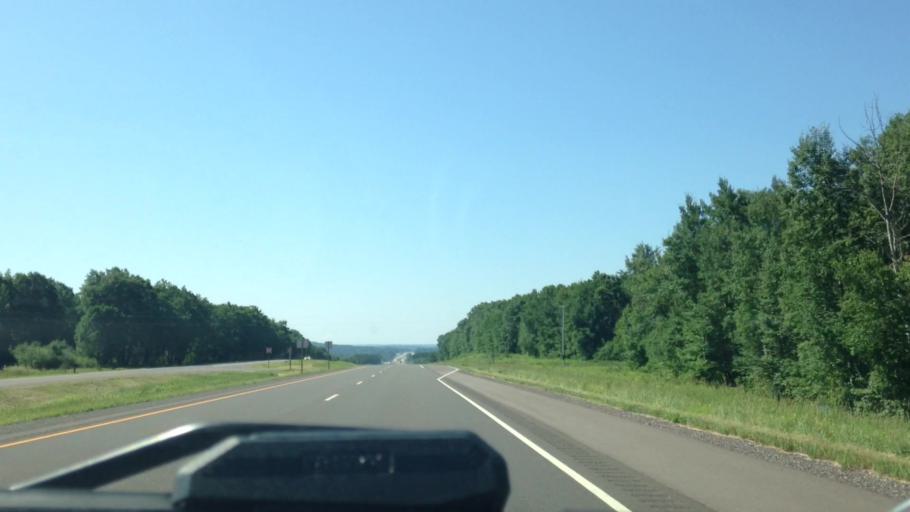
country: US
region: Wisconsin
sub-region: Washburn County
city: Spooner
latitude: 45.9367
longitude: -91.8281
